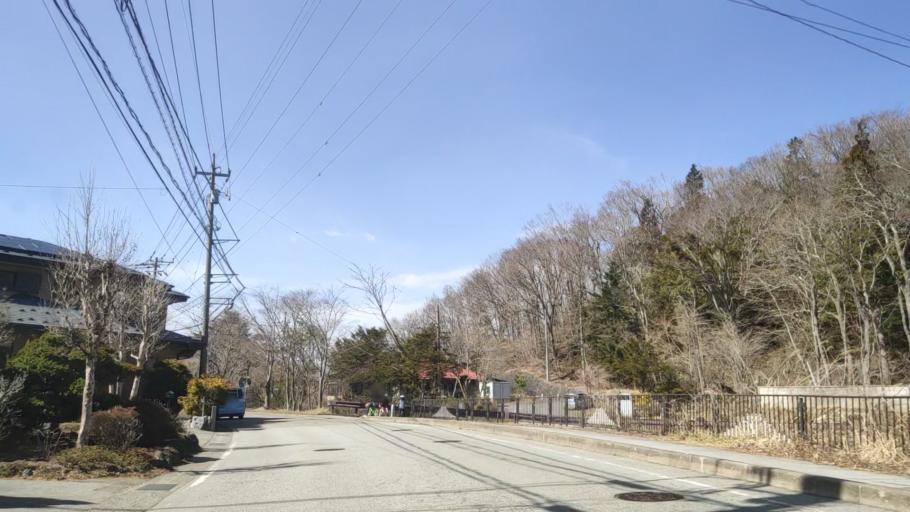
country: JP
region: Shizuoka
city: Gotemba
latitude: 35.4315
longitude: 138.8498
